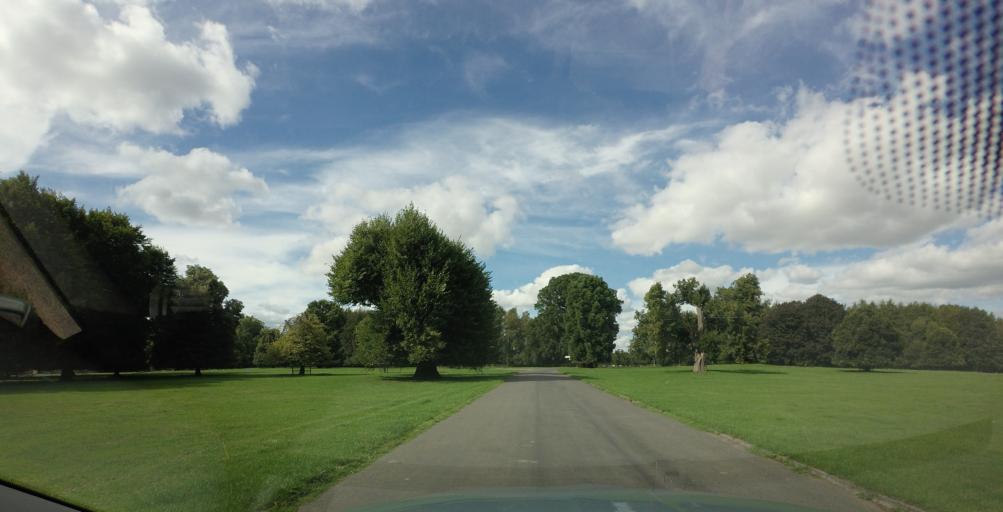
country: GB
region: England
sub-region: North Yorkshire
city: Ripon
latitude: 54.1020
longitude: -1.4669
